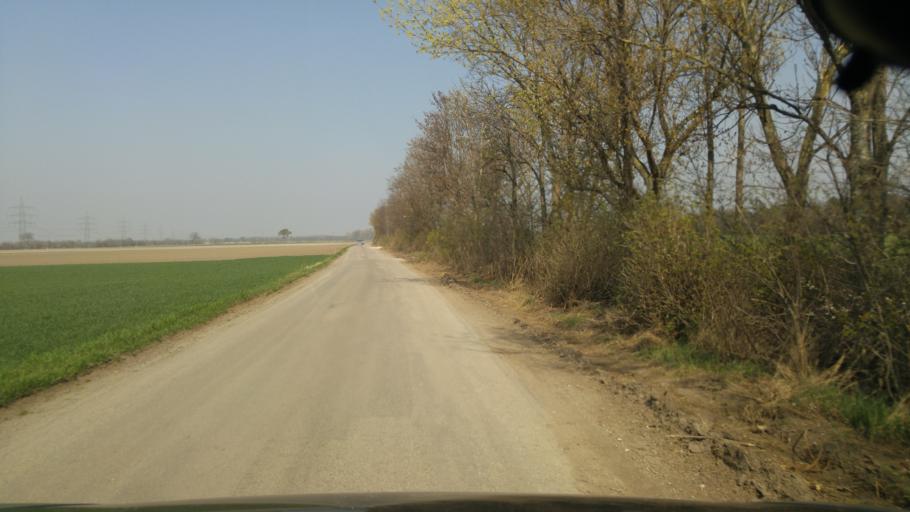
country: AT
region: Lower Austria
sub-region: Politischer Bezirk Modling
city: Munchendorf
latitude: 48.0307
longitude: 16.3950
